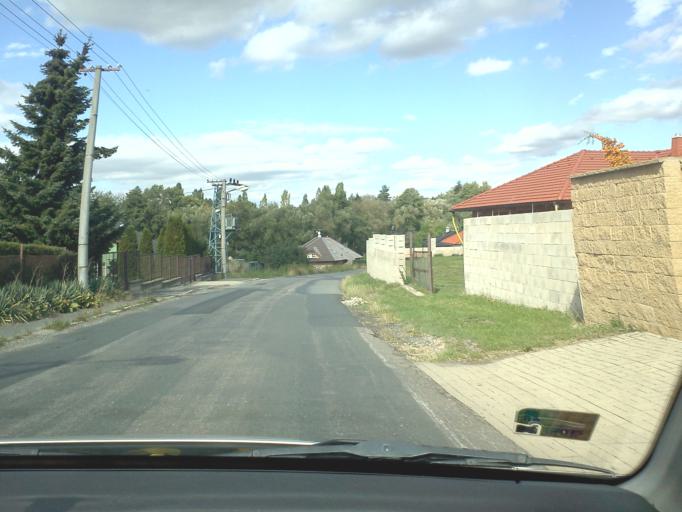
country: CZ
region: Central Bohemia
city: Mukarov
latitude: 50.0092
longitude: 14.7777
